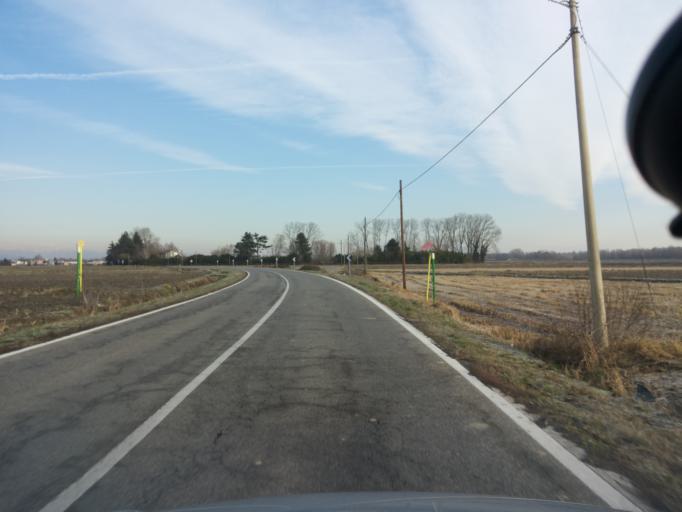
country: IT
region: Piedmont
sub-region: Provincia di Vercelli
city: Oldenico
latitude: 45.3923
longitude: 8.3787
